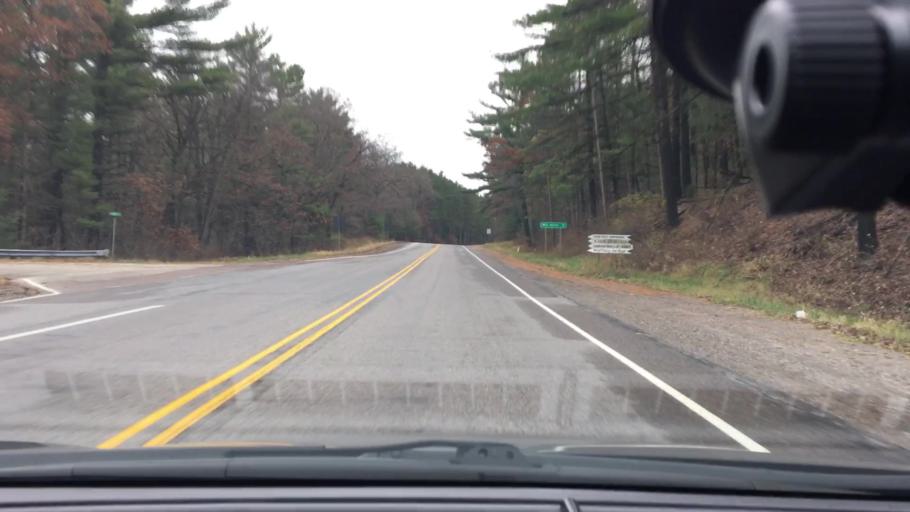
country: US
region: Wisconsin
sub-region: Columbia County
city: Wisconsin Dells
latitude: 43.6489
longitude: -89.8111
